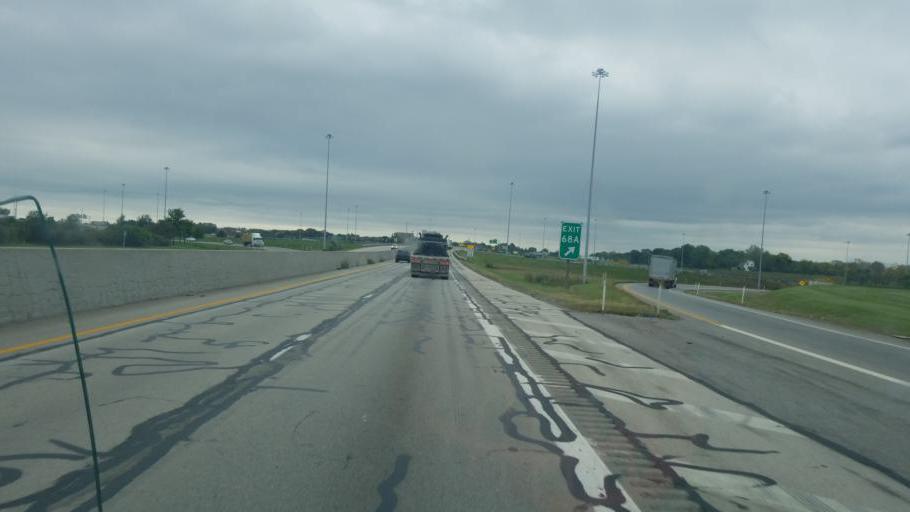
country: US
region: Ohio
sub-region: Lucas County
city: Maumee
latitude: 41.5506
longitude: -83.6901
